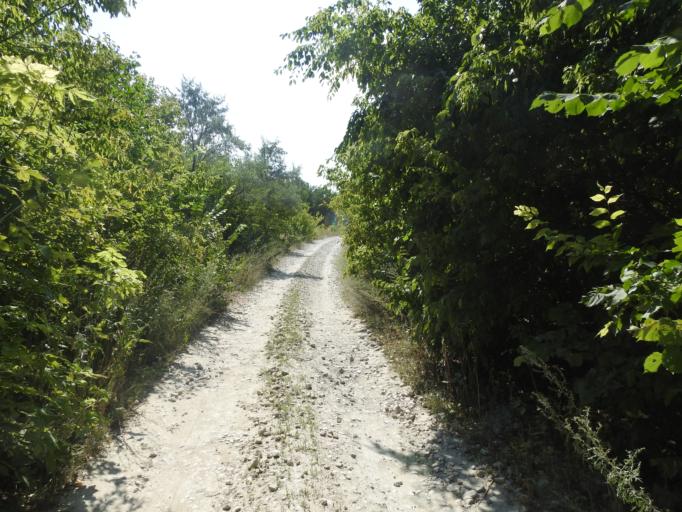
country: RU
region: Saratov
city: Rovnoye
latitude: 50.4875
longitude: 45.7210
